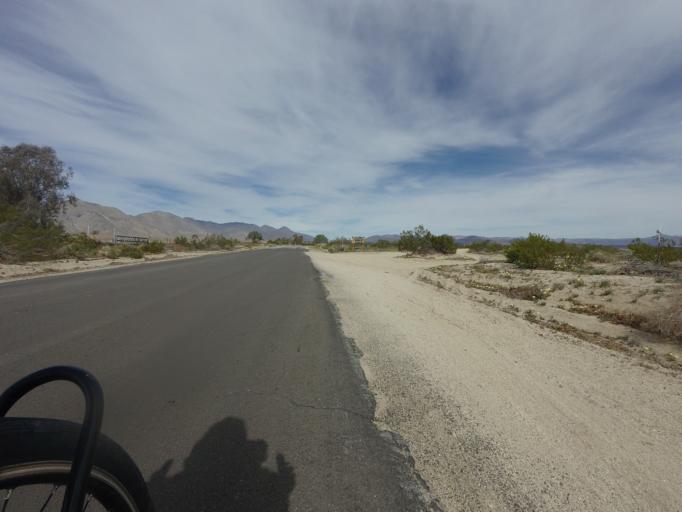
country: US
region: California
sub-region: Kern County
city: Inyokern
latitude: 35.7725
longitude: -117.8499
